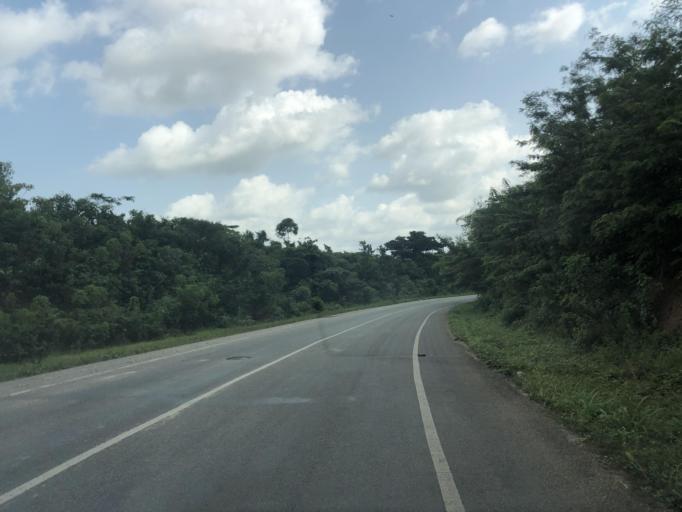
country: GH
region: Central
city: Cape Coast
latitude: 5.2269
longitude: -1.3243
